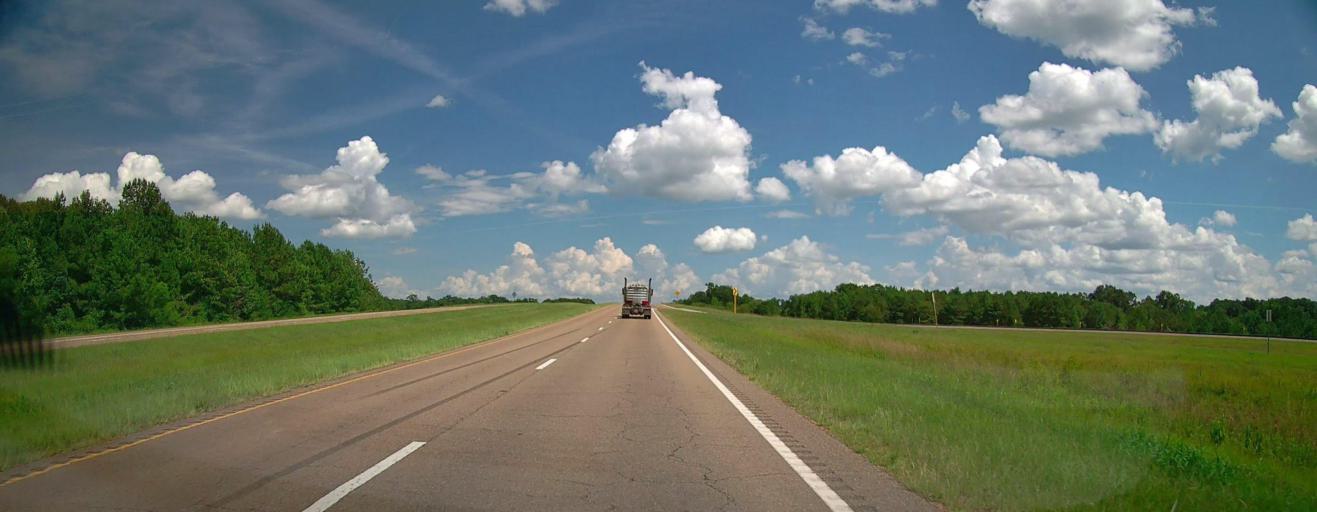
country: US
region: Mississippi
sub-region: Monroe County
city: Aberdeen
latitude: 33.8149
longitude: -88.4940
